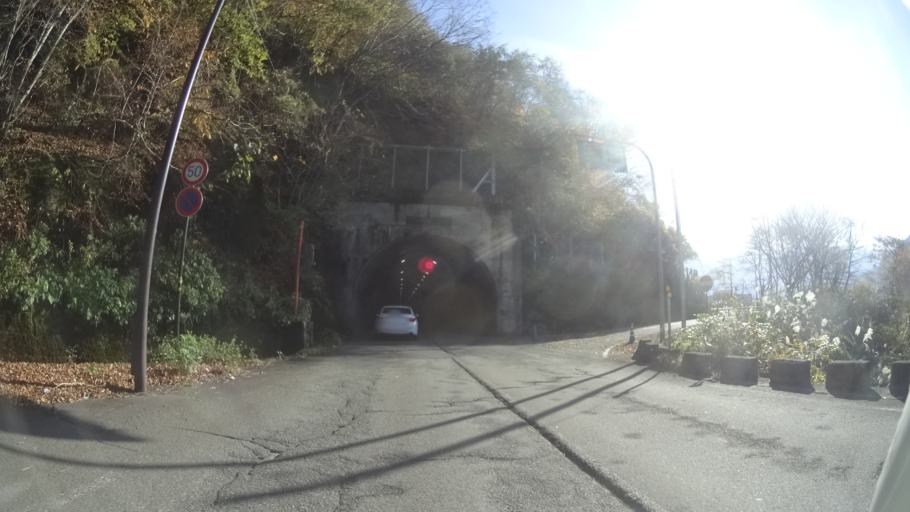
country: JP
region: Fukui
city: Ono
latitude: 35.8914
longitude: 136.6916
